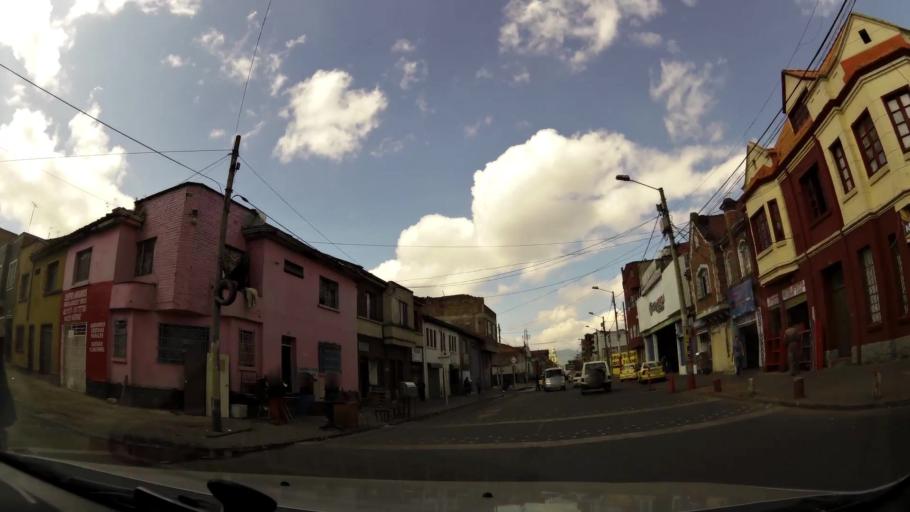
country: CO
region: Bogota D.C.
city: Bogota
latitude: 4.6121
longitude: -74.0781
